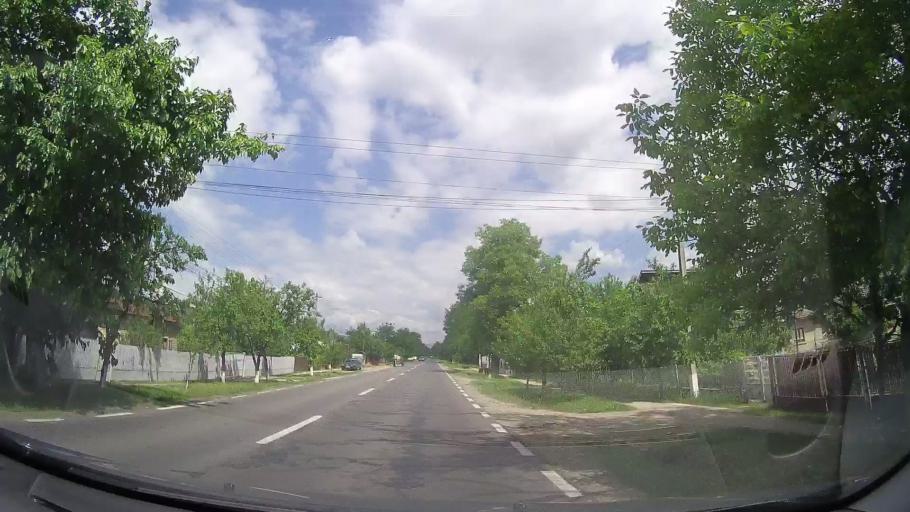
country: RO
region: Prahova
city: Drajna de Jos
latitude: 45.2169
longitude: 26.0362
